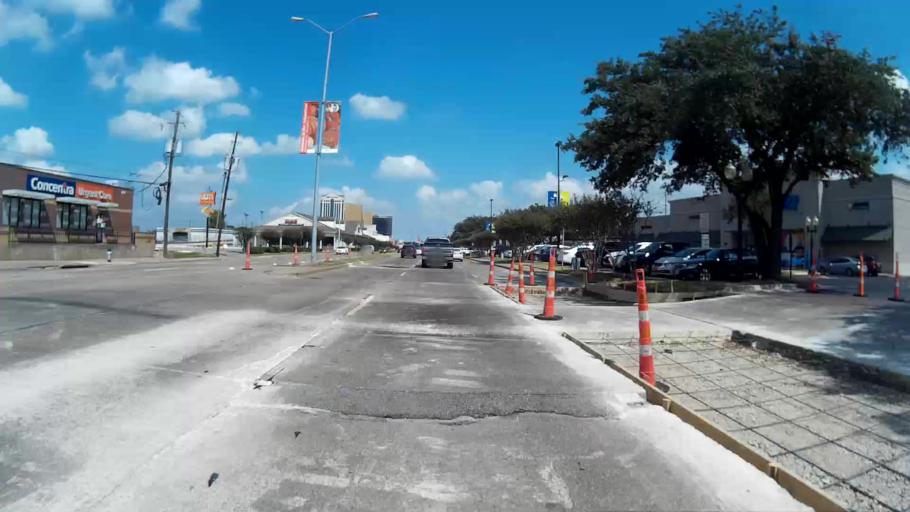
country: US
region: Texas
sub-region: Dallas County
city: Highland Park
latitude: 32.8541
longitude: -96.7692
